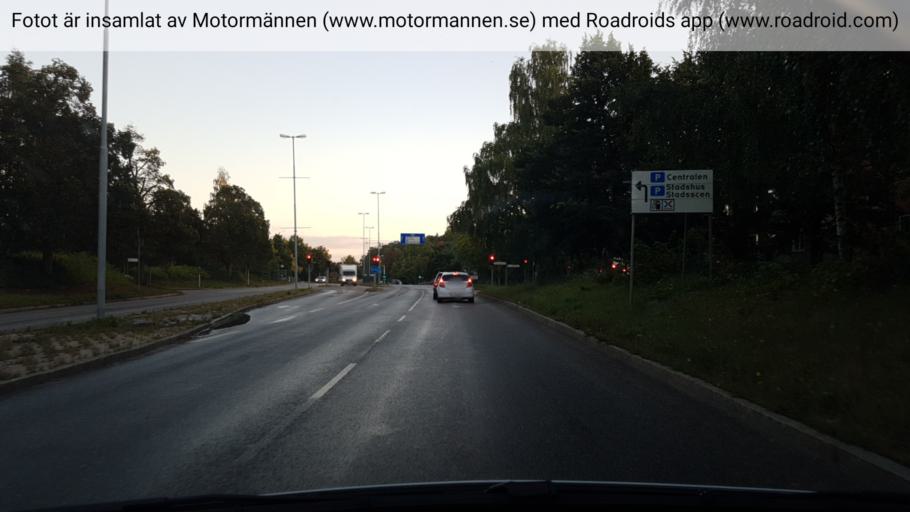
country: SE
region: Stockholm
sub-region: Sodertalje Kommun
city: Soedertaelje
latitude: 59.1903
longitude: 17.6262
